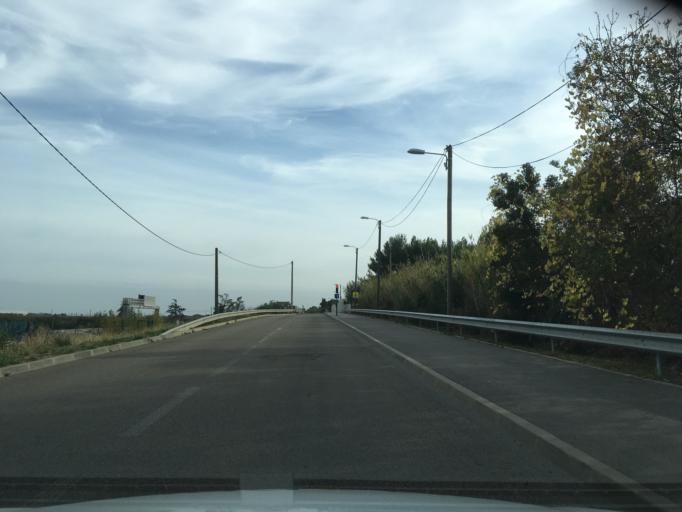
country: FR
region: Languedoc-Roussillon
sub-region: Departement de l'Herault
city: Lattes
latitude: 43.6013
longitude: 3.9181
